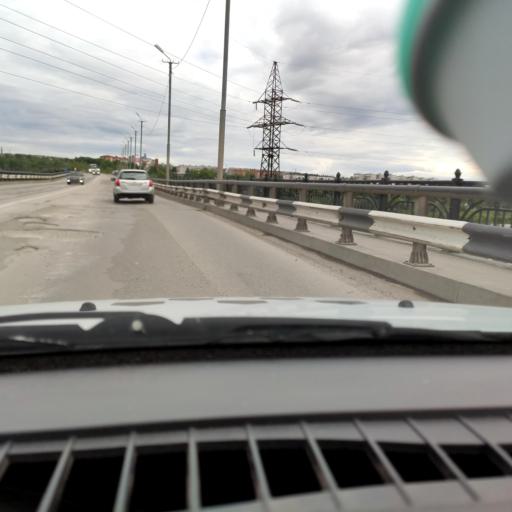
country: RU
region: Perm
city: Chusovoy
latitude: 58.2885
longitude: 57.8122
